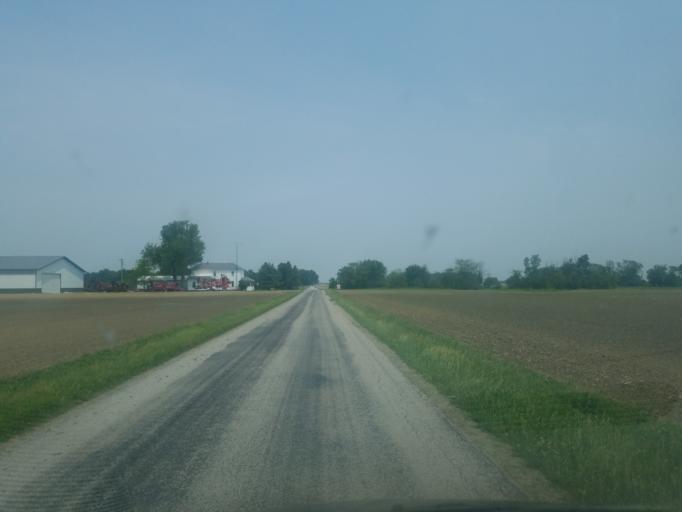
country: US
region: Ohio
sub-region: Marion County
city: Marion
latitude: 40.6959
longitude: -83.1113
